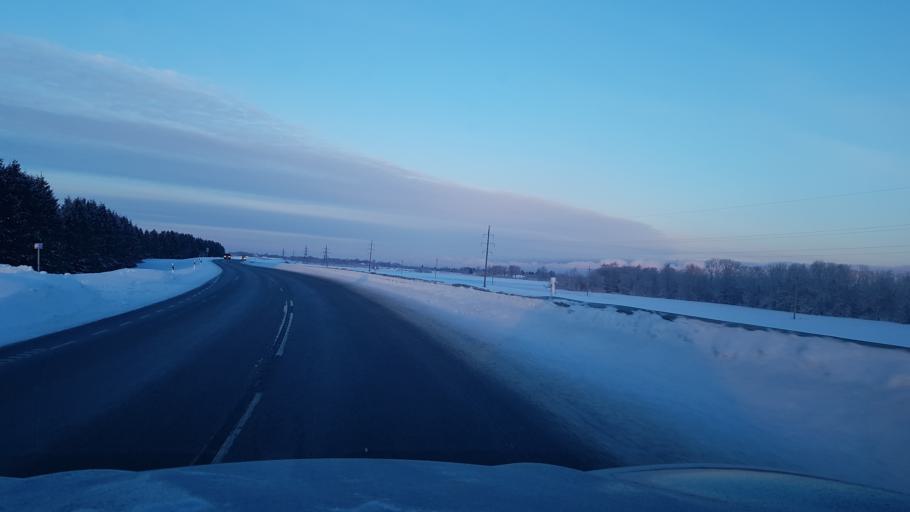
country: EE
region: Ida-Virumaa
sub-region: Narva-Joesuu linn
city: Narva-Joesuu
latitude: 59.4043
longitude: 28.0506
